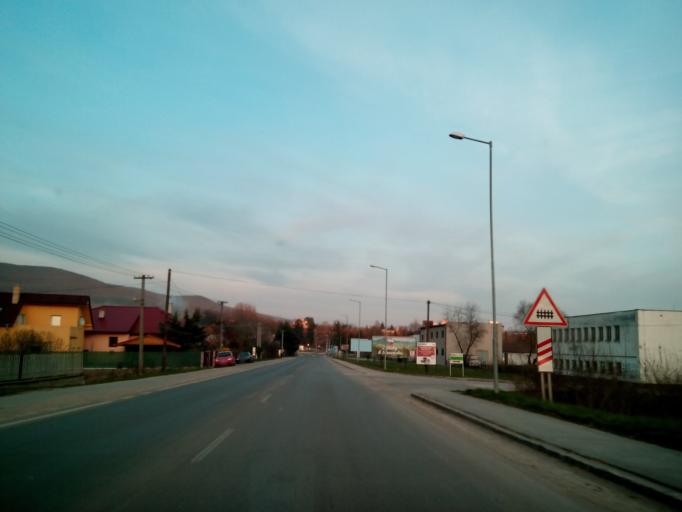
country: SK
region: Kosicky
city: Roznava
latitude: 48.6605
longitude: 20.5166
